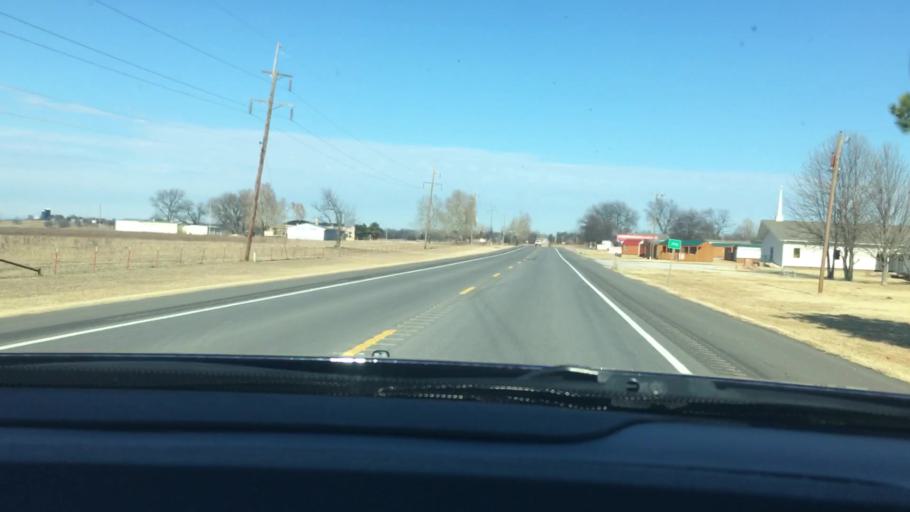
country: US
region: Oklahoma
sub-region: Garvin County
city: Wynnewood
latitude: 34.5905
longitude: -97.1425
